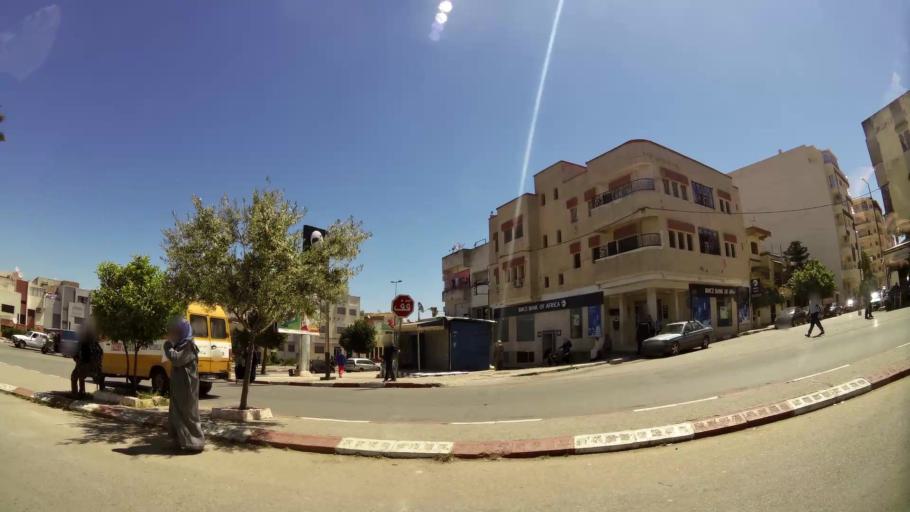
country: MA
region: Meknes-Tafilalet
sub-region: Meknes
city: Meknes
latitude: 33.9069
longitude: -5.5327
